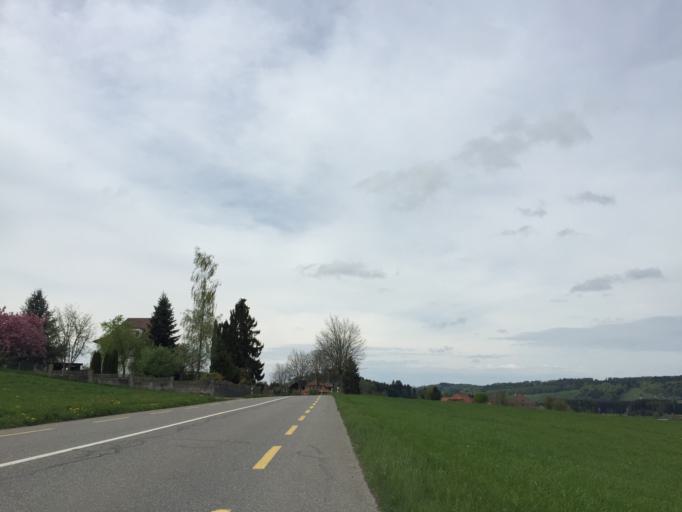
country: CH
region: Bern
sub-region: Bern-Mittelland District
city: Rubigen
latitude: 46.9115
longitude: 7.5286
